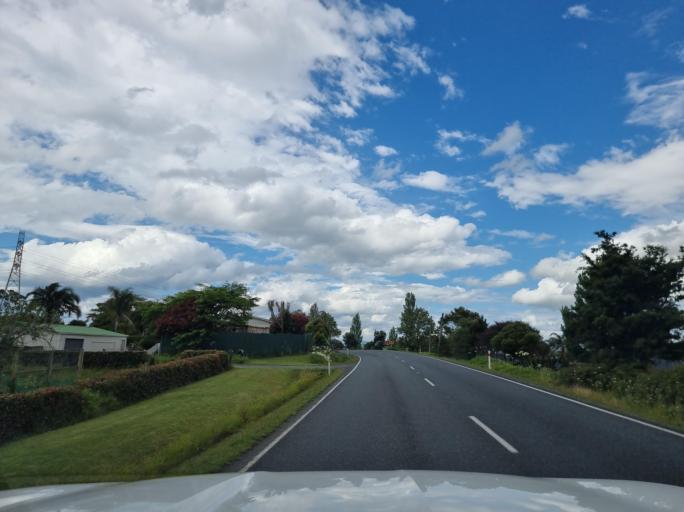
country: NZ
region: Northland
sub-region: Whangarei
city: Whangarei
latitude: -35.8431
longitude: 174.2973
